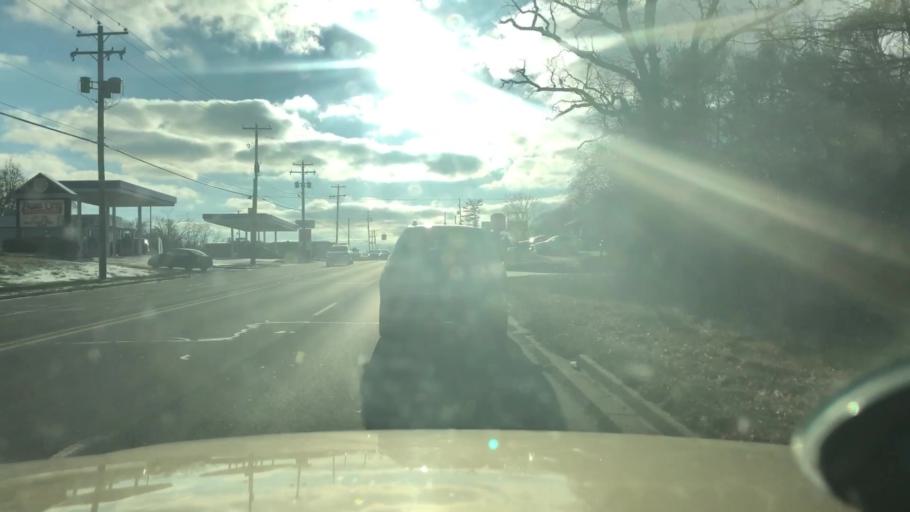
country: US
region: Michigan
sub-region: Jackson County
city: Vandercook Lake
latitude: 42.2028
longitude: -84.4358
